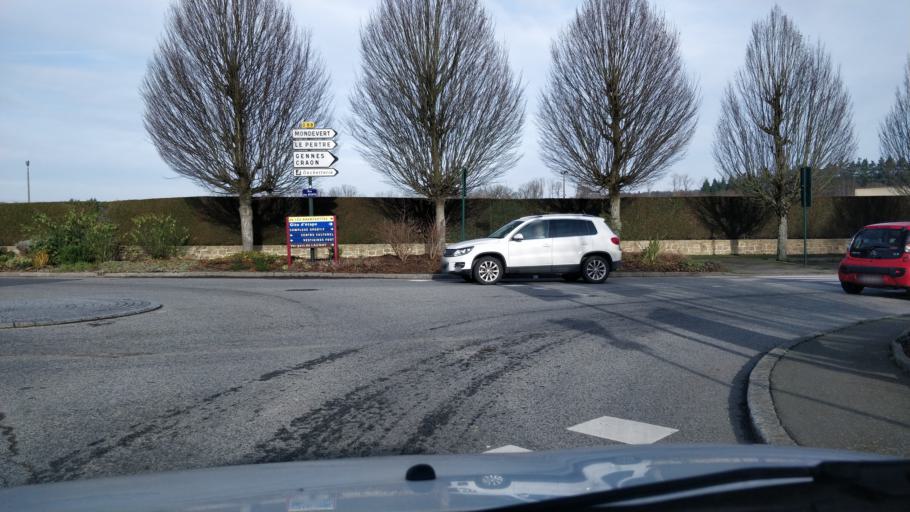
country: FR
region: Brittany
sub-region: Departement d'Ille-et-Vilaine
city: Argentre-du-Plessis
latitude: 48.0580
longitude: -1.1559
